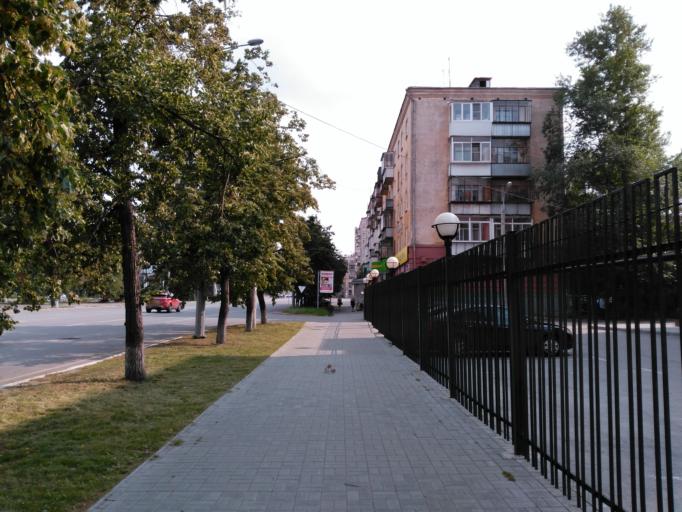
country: RU
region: Chelyabinsk
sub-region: Gorod Chelyabinsk
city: Chelyabinsk
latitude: 55.1648
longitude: 61.4109
